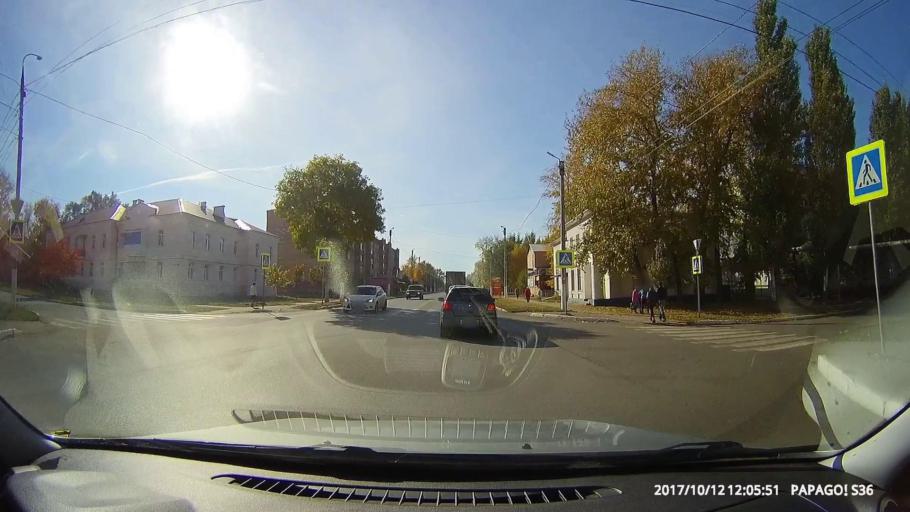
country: RU
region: Samara
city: Chapayevsk
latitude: 52.9754
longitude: 49.7101
